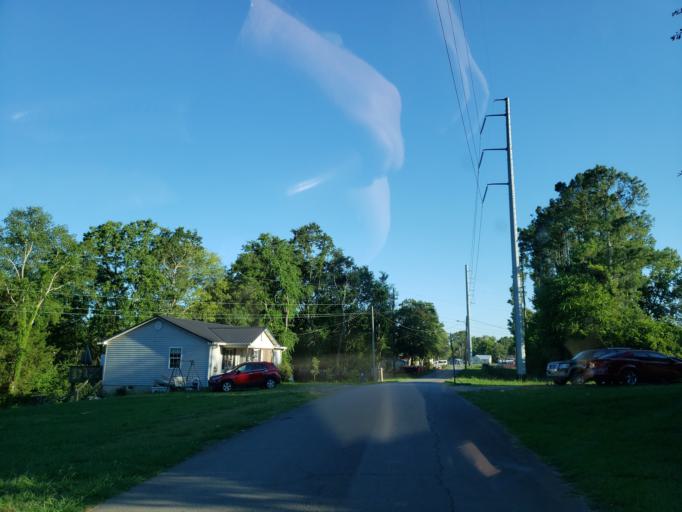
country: US
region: Georgia
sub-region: Polk County
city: Aragon
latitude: 34.0423
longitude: -85.0544
